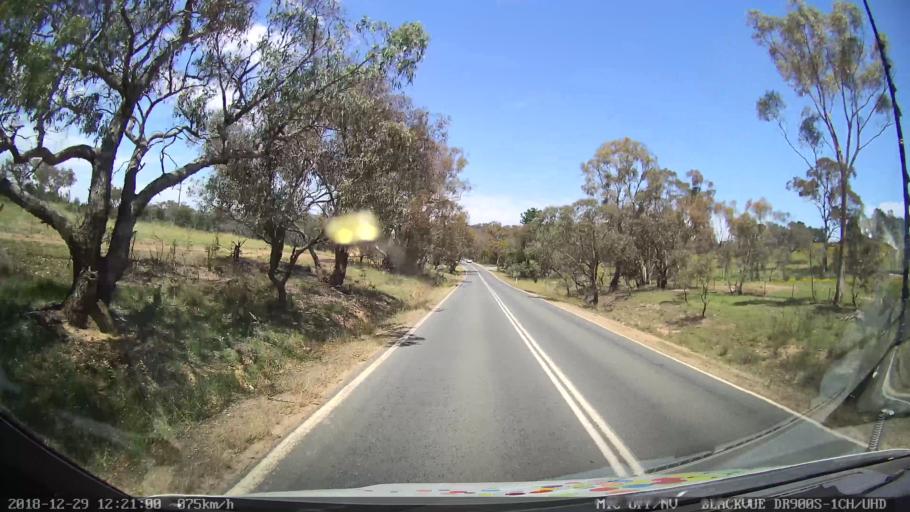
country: AU
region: New South Wales
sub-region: Queanbeyan
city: Queanbeyan
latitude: -35.4089
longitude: 149.2262
